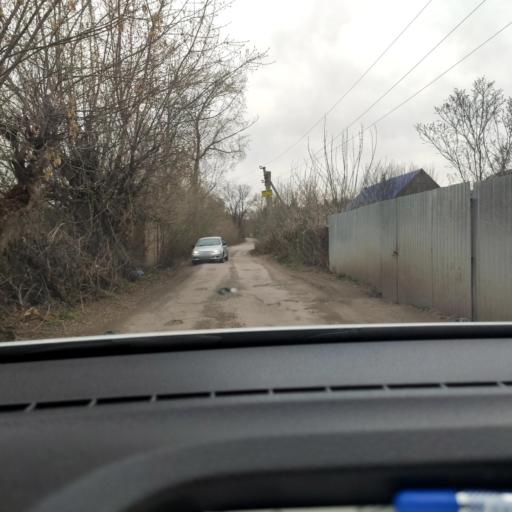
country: RU
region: Bashkortostan
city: Avdon
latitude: 54.6249
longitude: 55.5965
